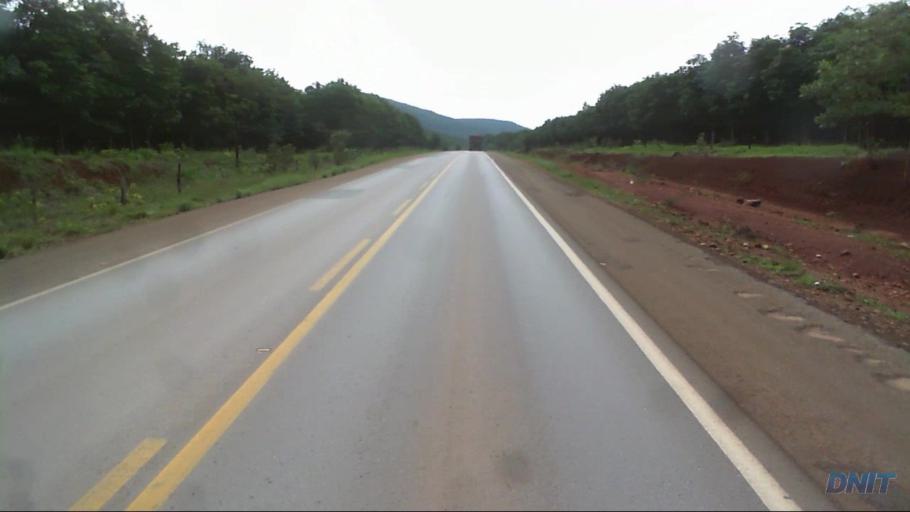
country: BR
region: Goias
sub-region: Barro Alto
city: Barro Alto
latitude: -14.8818
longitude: -48.9874
